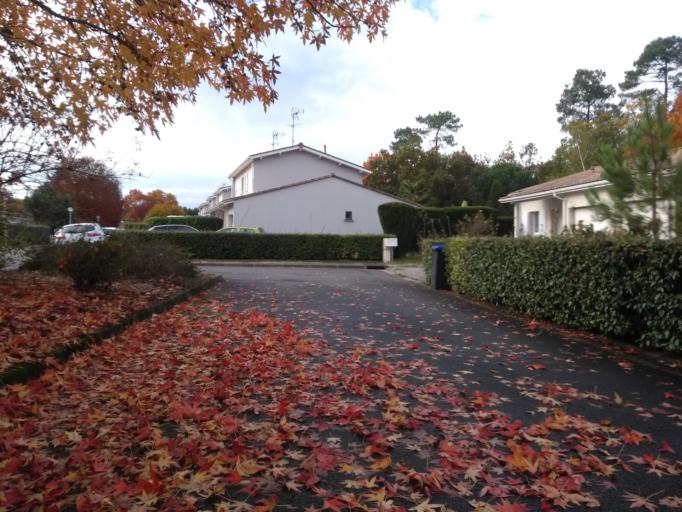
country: FR
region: Aquitaine
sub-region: Departement de la Gironde
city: Cestas
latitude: 44.7400
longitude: -0.6731
